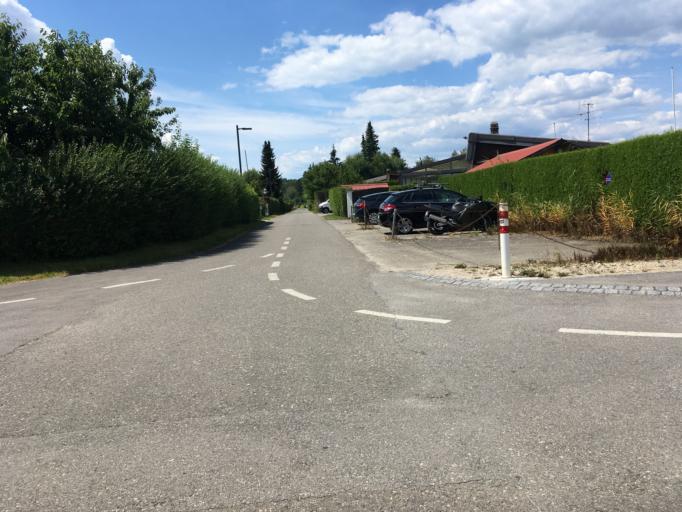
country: CH
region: Vaud
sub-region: Broye-Vully District
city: Payerne
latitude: 46.9062
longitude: 6.9337
